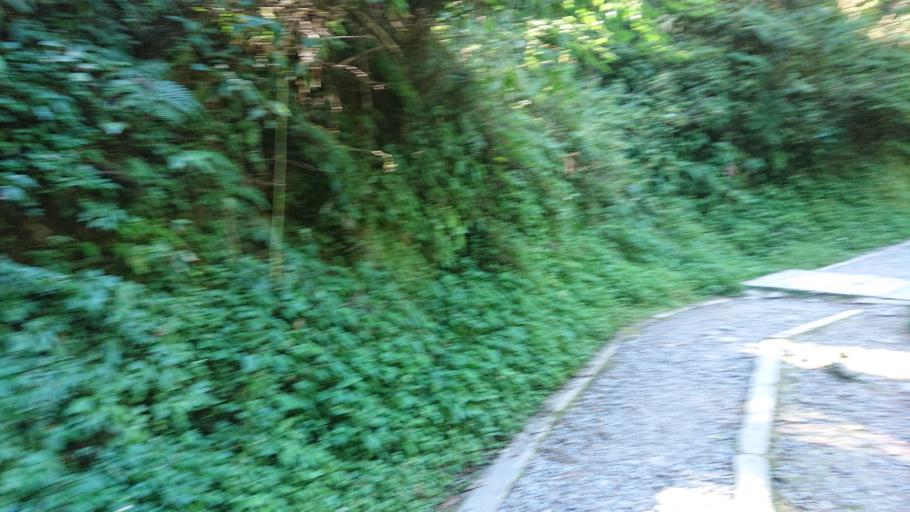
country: TW
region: Taiwan
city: Lugu
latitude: 23.4824
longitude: 120.8277
